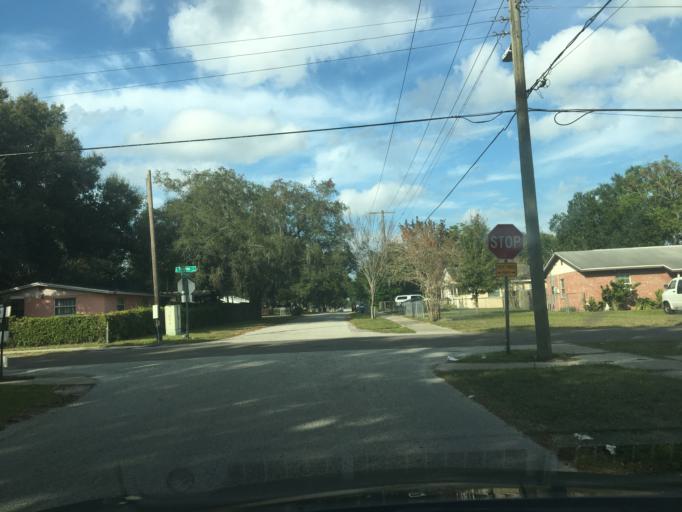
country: US
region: Florida
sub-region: Hillsborough County
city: Temple Terrace
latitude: 28.0251
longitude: -82.4145
